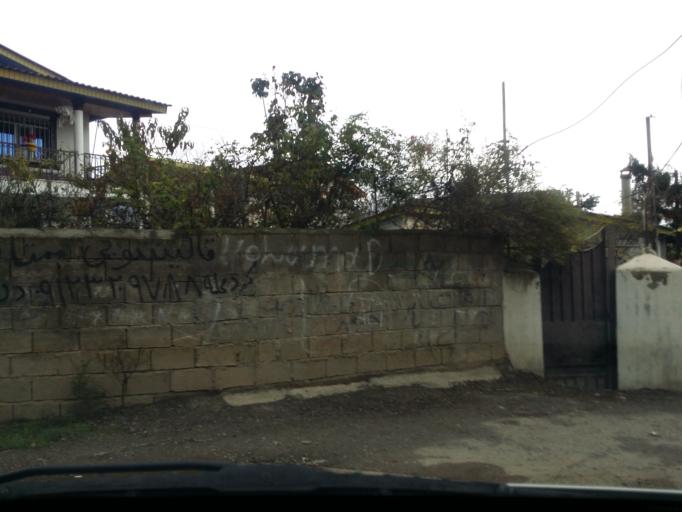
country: IR
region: Mazandaran
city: `Abbasabad
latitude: 36.5035
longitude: 51.1848
